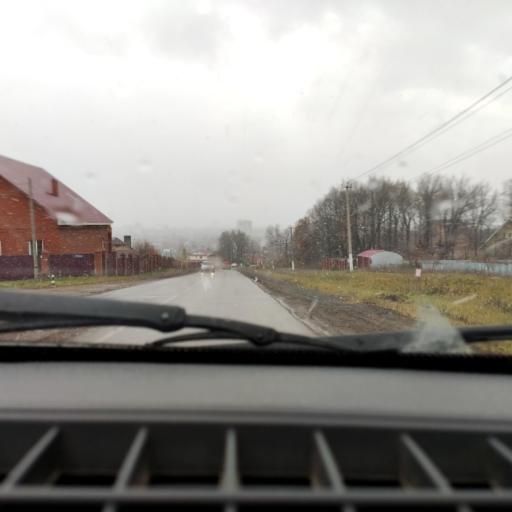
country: RU
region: Bashkortostan
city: Mikhaylovka
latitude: 54.8115
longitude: 55.8822
